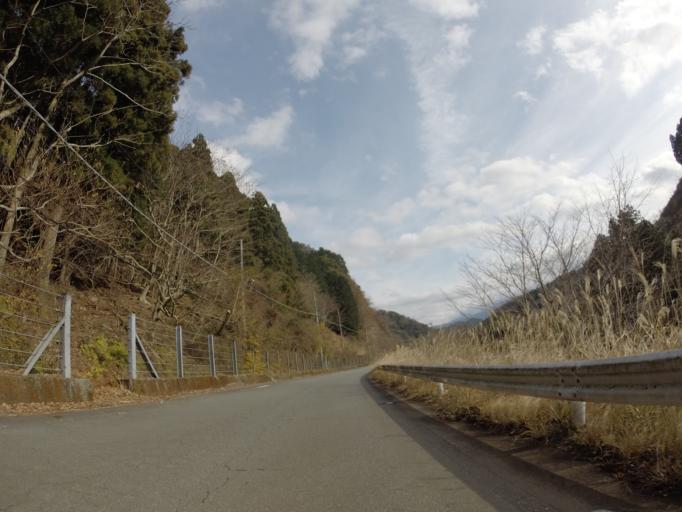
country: JP
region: Shizuoka
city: Heda
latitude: 34.8932
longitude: 138.8772
